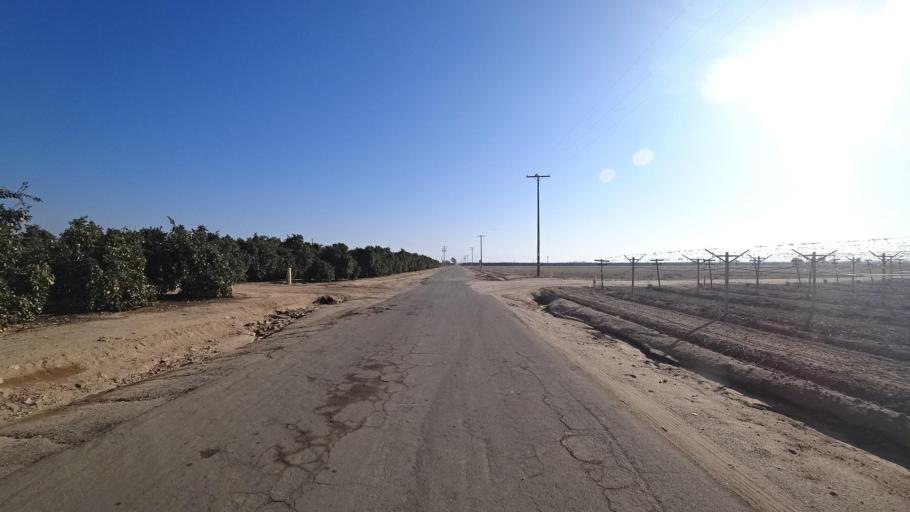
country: US
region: California
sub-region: Tulare County
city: Richgrove
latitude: 35.7253
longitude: -119.1519
